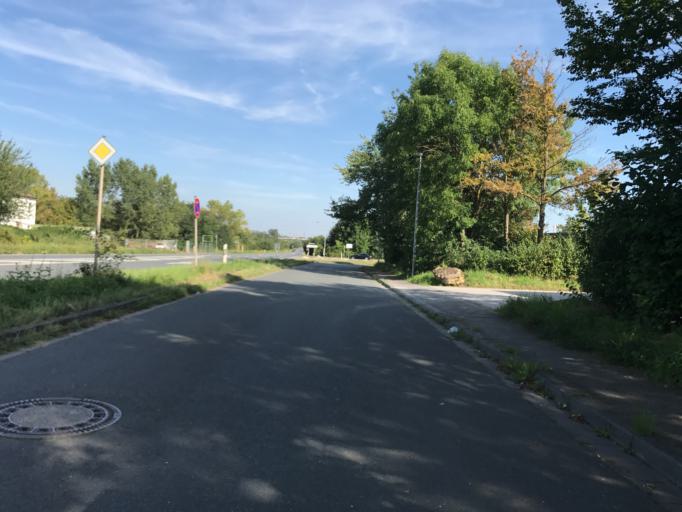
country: DE
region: Rheinland-Pfalz
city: Budenheim
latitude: 50.0278
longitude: 8.1976
